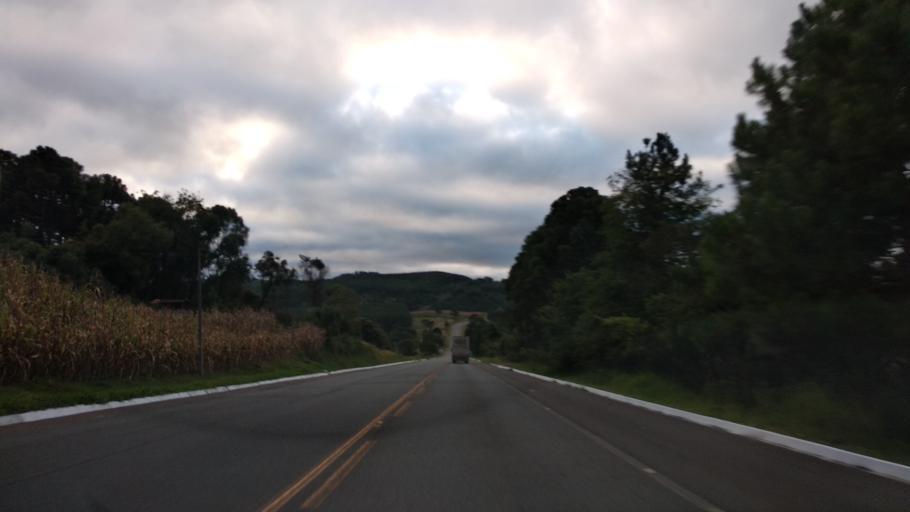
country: BR
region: Santa Catarina
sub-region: Campos Novos
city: Campos Novos
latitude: -27.4953
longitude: -50.9624
